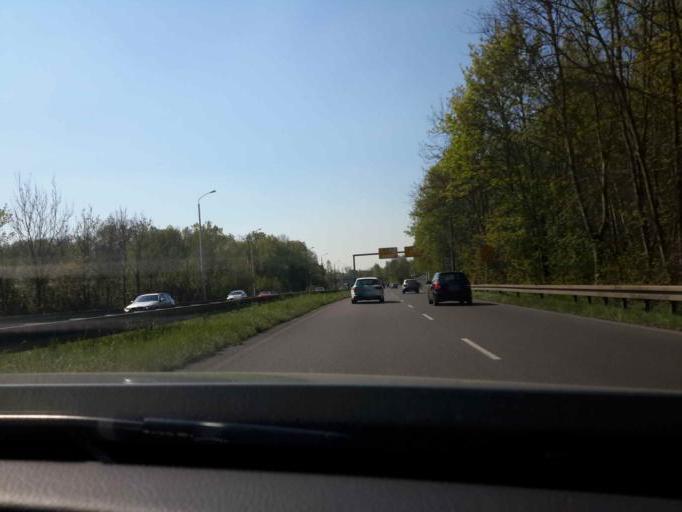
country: DE
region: Saxony
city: Markkleeberg
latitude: 51.2920
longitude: 12.3780
